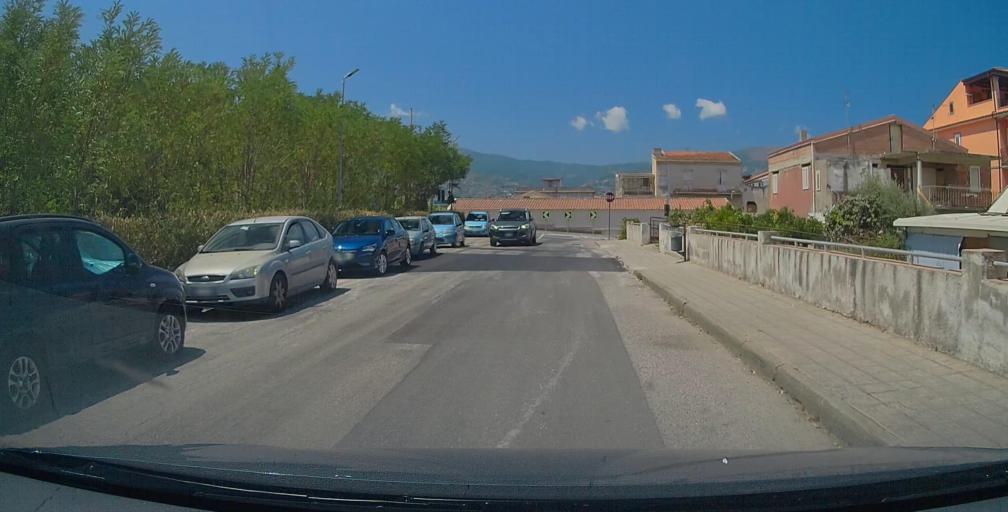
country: IT
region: Sicily
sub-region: Messina
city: Oliveri
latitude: 38.1469
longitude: 15.0152
